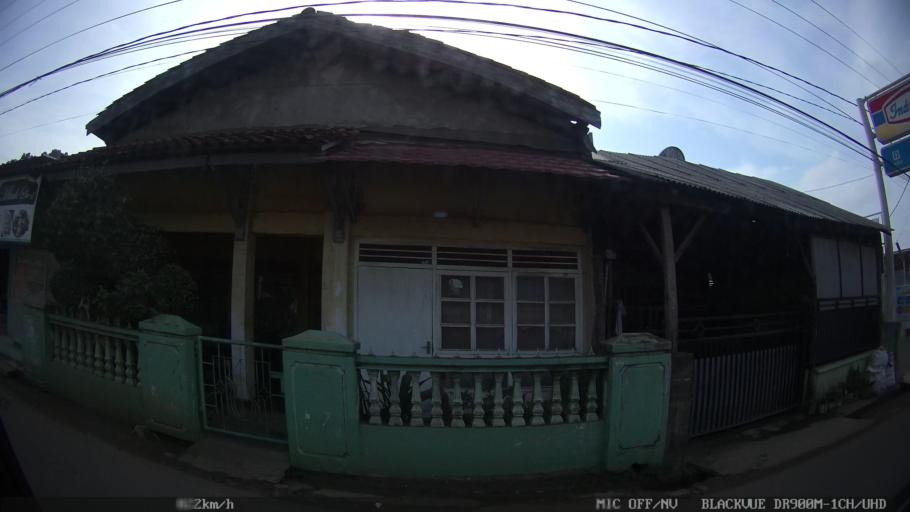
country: ID
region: Lampung
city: Kedaton
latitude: -5.3918
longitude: 105.2664
